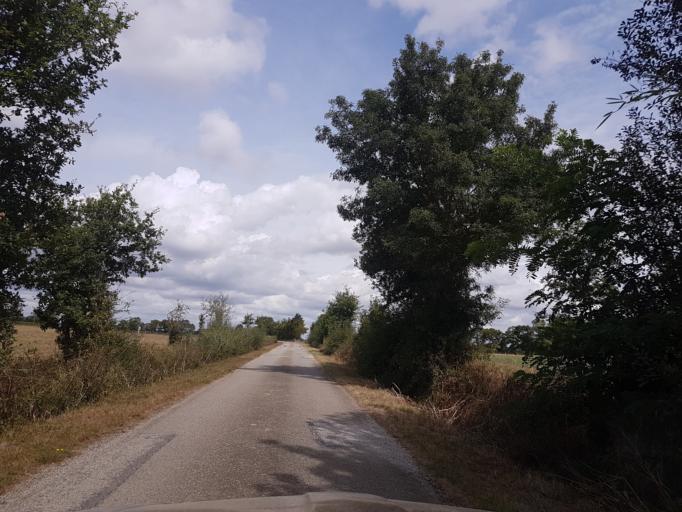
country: FR
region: Pays de la Loire
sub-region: Departement de la Loire-Atlantique
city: Petit-Mars
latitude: 47.4144
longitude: -1.4467
